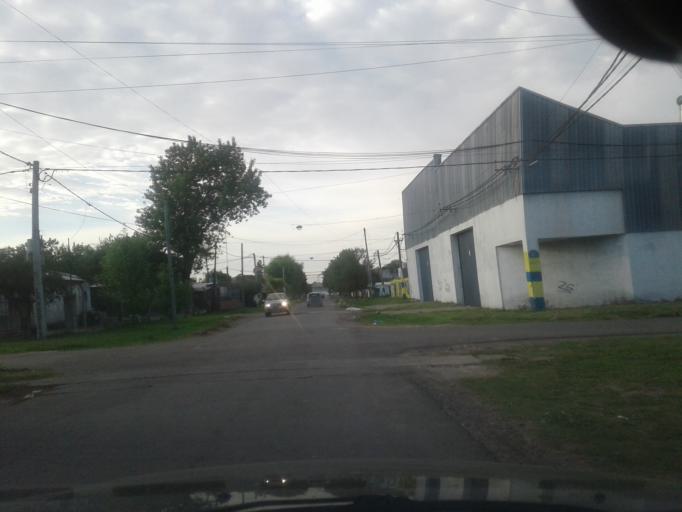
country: AR
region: Santa Fe
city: Granadero Baigorria
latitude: -32.8861
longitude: -60.7259
